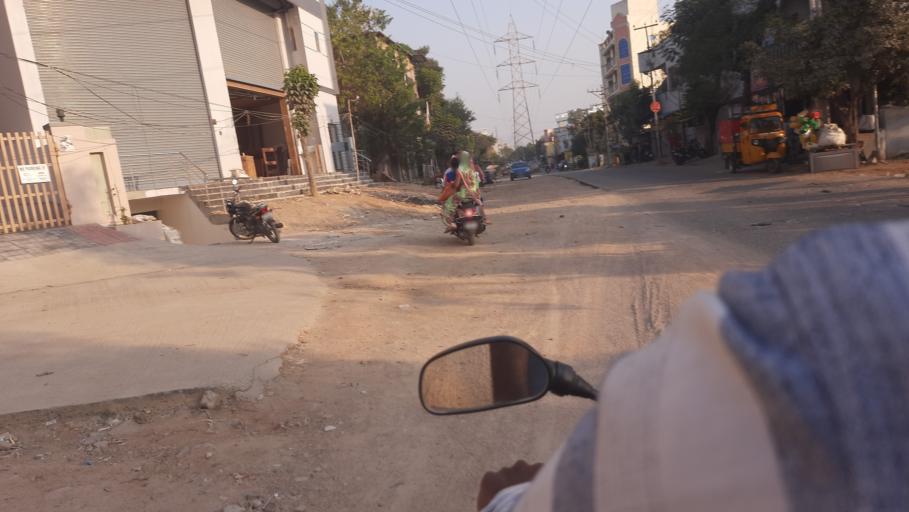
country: IN
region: Telangana
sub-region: Rangareddi
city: Secunderabad
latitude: 17.4991
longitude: 78.5410
